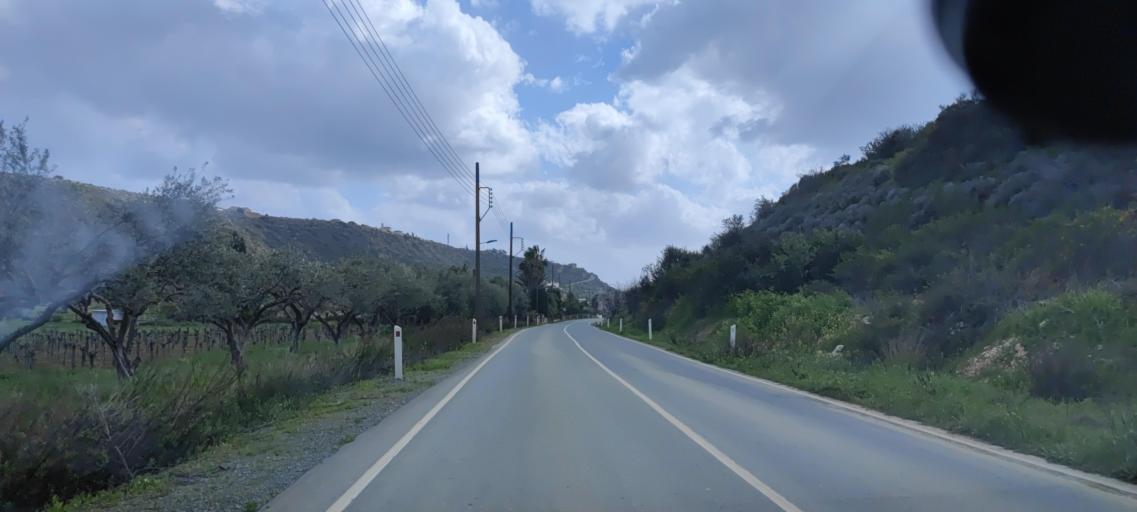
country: CY
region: Limassol
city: Pissouri
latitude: 34.6635
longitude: 32.7279
